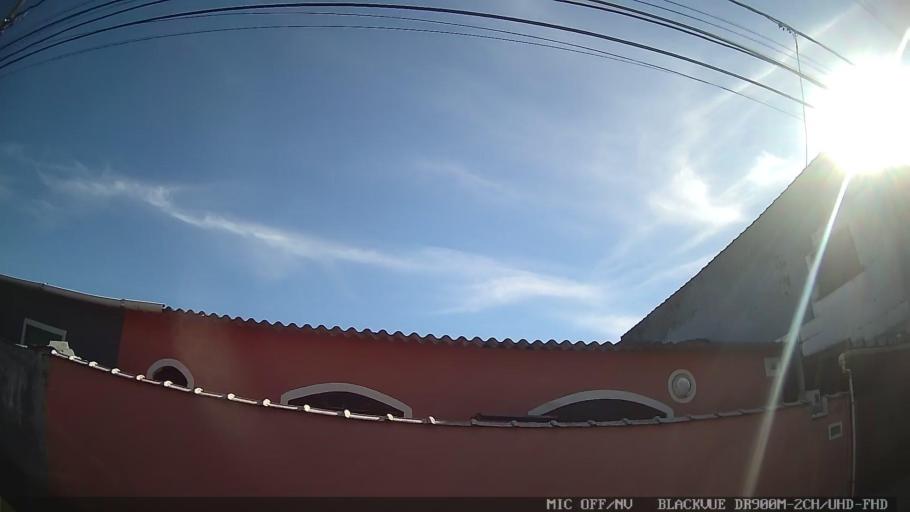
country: BR
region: Sao Paulo
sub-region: Santos
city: Santos
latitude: -23.9358
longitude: -46.2872
